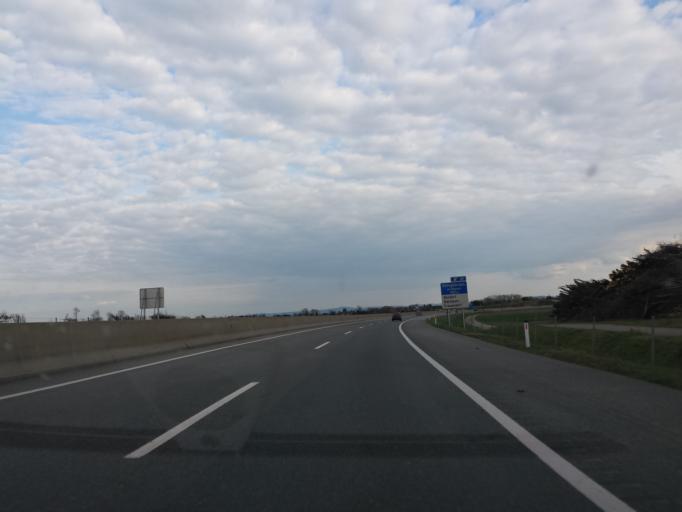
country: AT
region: Lower Austria
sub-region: Politischer Bezirk Tulln
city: Kirchberg am Wagram
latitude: 48.3985
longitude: 15.9115
